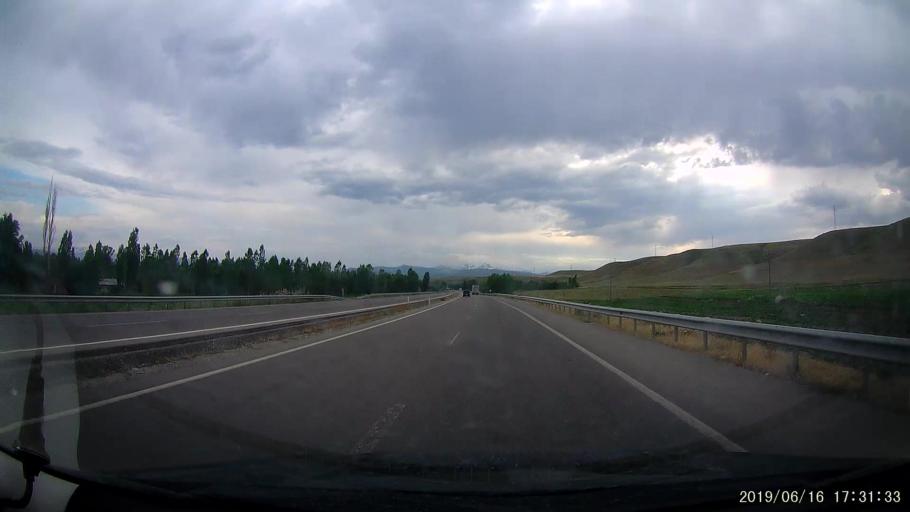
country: TR
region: Erzincan
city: Tercan
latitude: 39.7730
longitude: 40.3201
